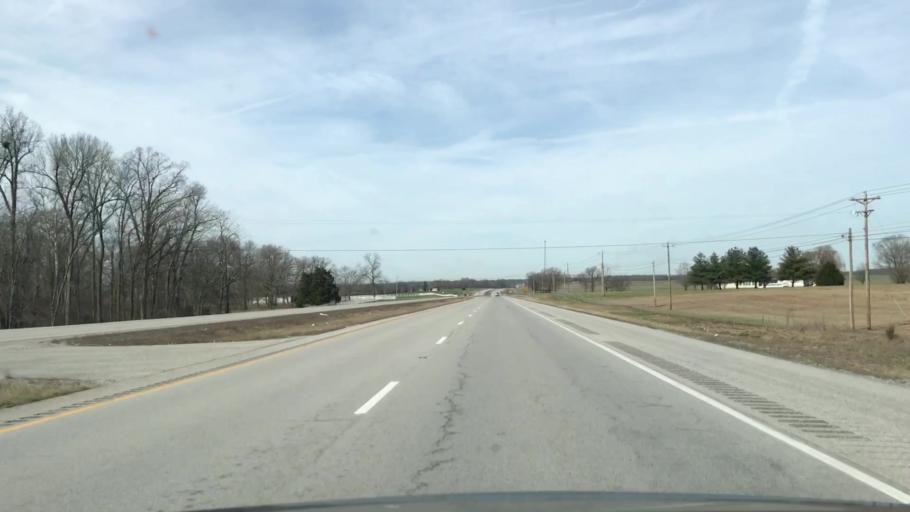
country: US
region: Kentucky
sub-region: Christian County
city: Hopkinsville
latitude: 36.8793
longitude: -87.5760
